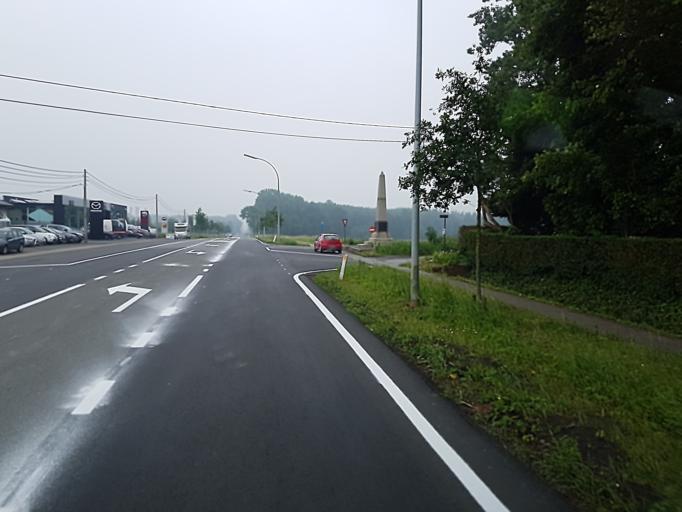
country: BE
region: Flanders
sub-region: Provincie West-Vlaanderen
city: Zonnebeke
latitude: 50.8435
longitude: 2.9613
